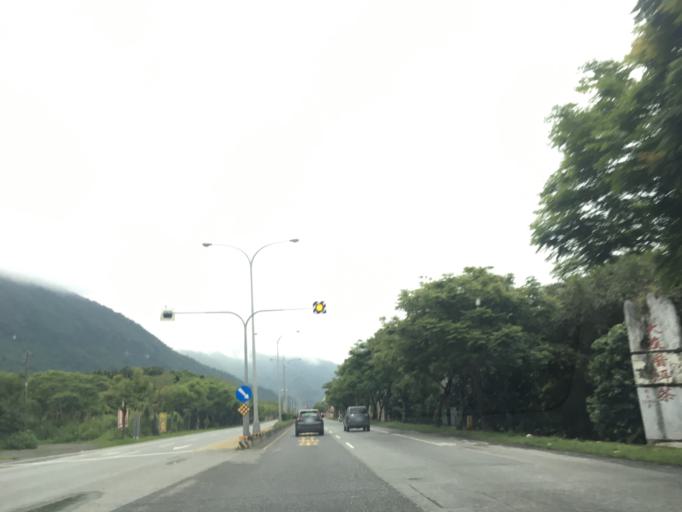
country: TW
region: Taiwan
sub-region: Hualien
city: Hualian
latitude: 24.0666
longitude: 121.6076
